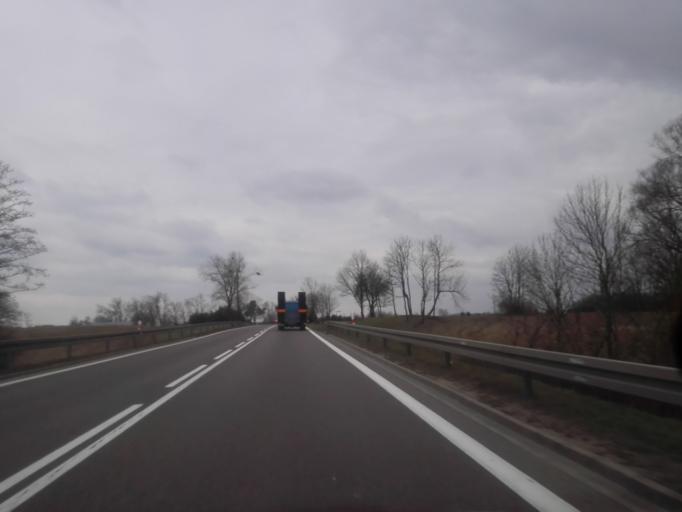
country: PL
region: Podlasie
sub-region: Powiat augustowski
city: Augustow
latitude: 53.7994
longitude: 22.8840
